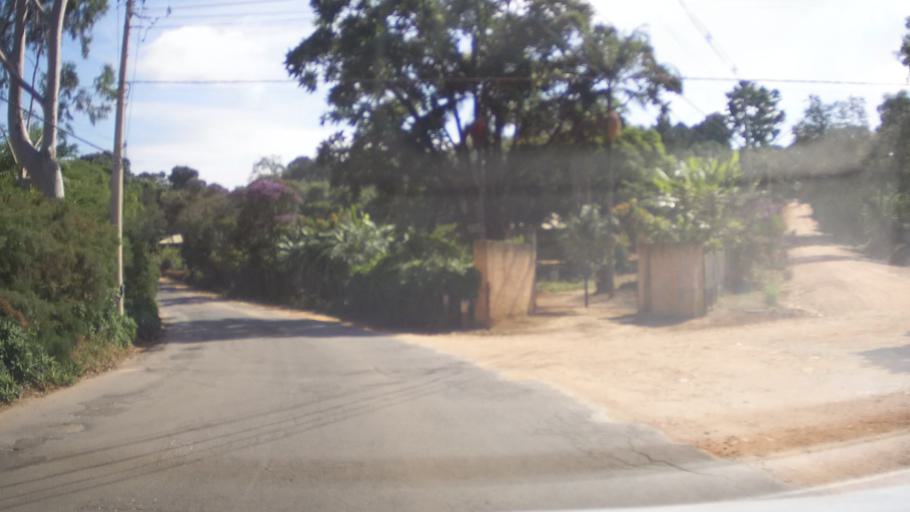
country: BR
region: Sao Paulo
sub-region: Itupeva
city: Itupeva
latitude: -23.2118
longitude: -47.0674
